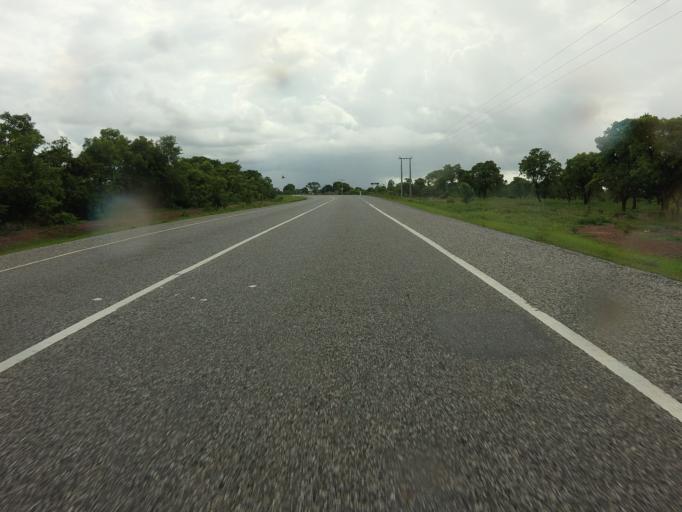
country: GH
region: Northern
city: Tamale
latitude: 9.1350
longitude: -1.3339
